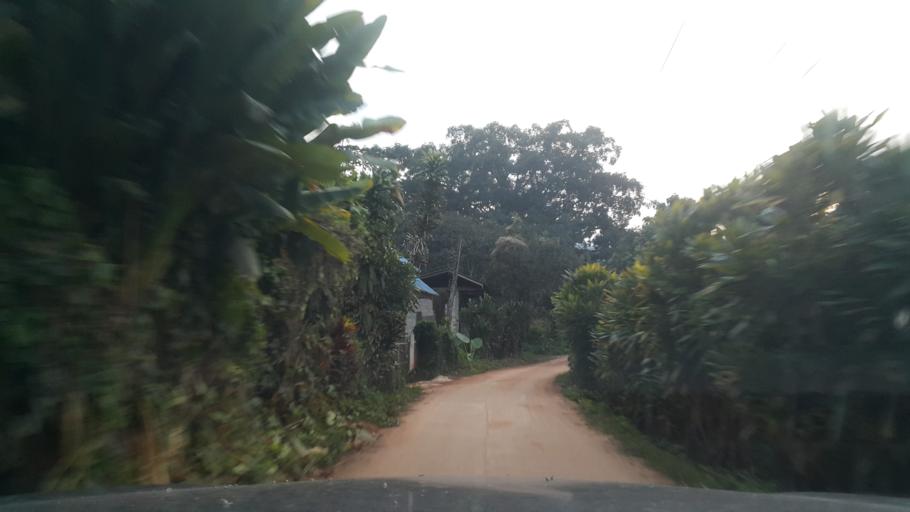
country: TH
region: Chiang Mai
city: Samoeng
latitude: 18.9508
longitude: 98.6754
